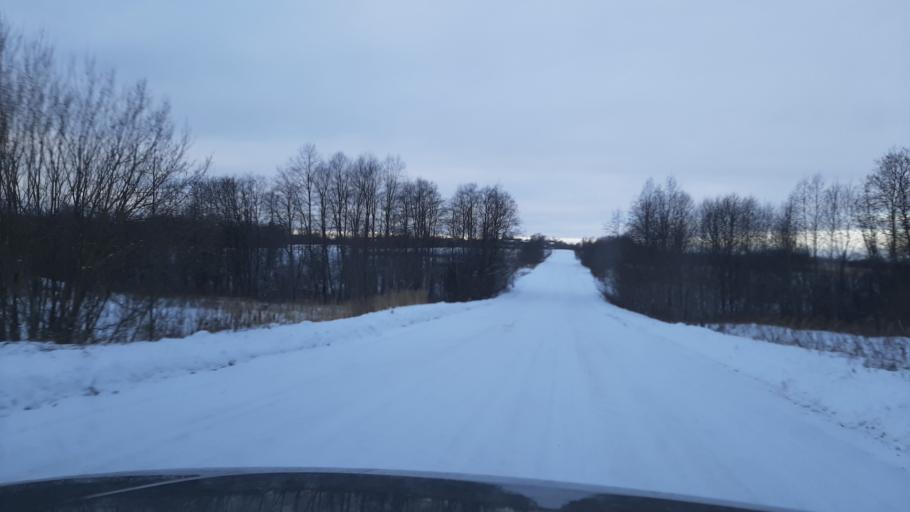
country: RU
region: Kostroma
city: Volgorechensk
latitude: 57.4483
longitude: 40.9838
